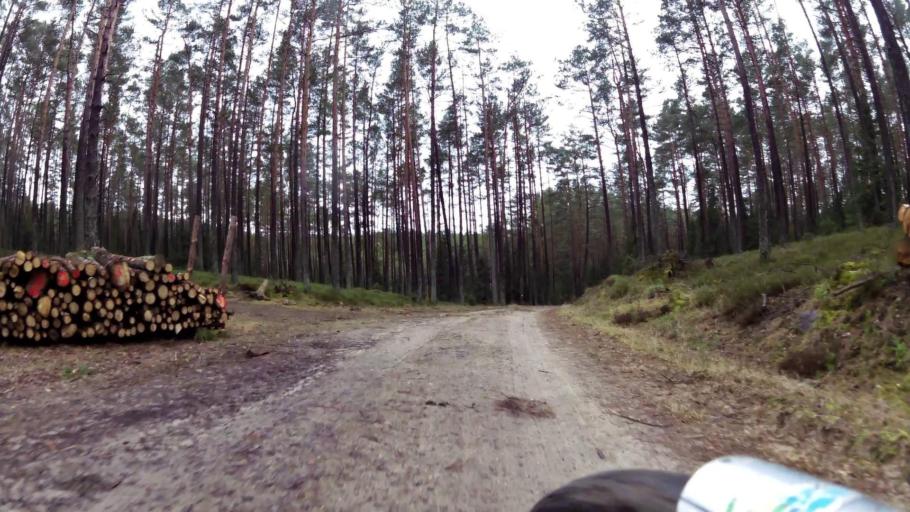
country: PL
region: Pomeranian Voivodeship
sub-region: Powiat bytowski
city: Borzytuchom
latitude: 54.2597
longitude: 17.3835
